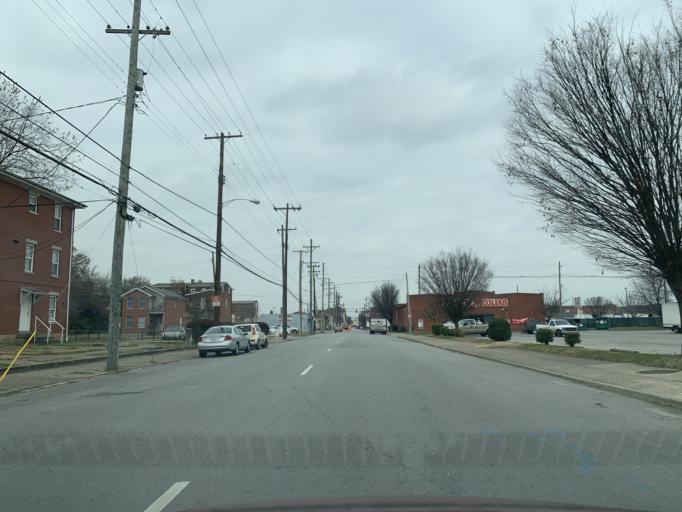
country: US
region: Kentucky
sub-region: Jefferson County
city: Louisville
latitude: 38.2559
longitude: -85.7752
